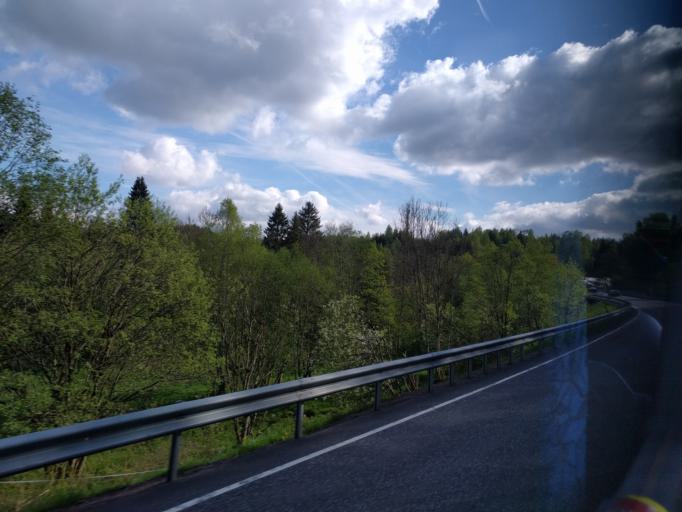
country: NO
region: Vestfold
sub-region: Lardal
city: Svarstad
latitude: 59.3338
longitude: 9.8936
